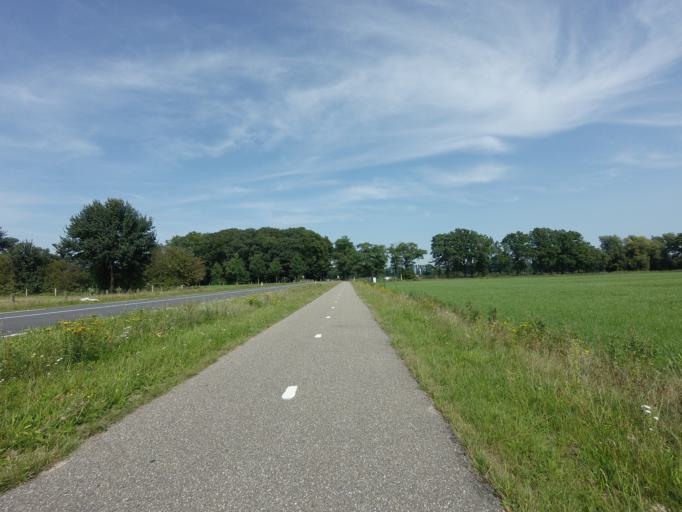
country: NL
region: Overijssel
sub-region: Gemeente Borne
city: Borne
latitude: 52.3306
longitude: 6.7273
